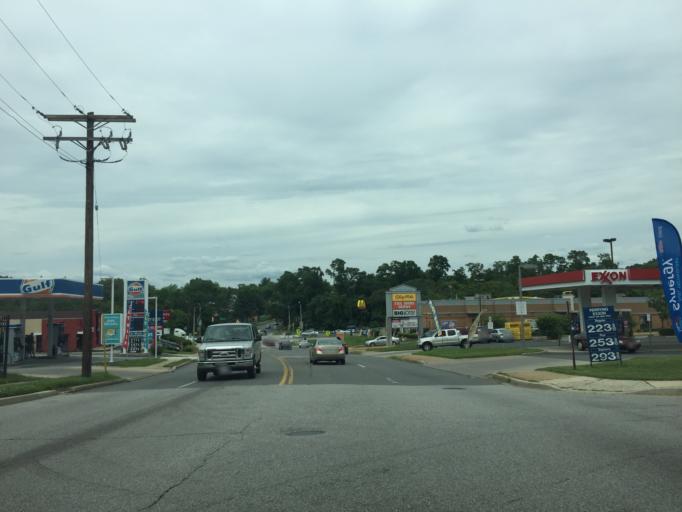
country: US
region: Maryland
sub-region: Baltimore County
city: Parkville
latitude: 39.3718
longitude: -76.5671
